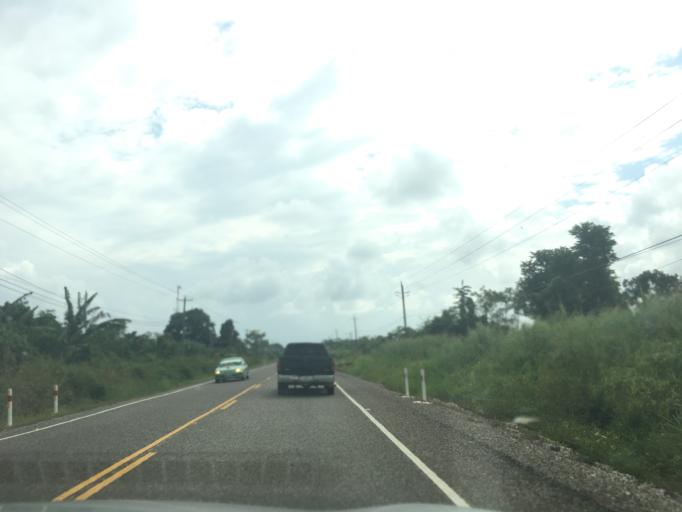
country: BZ
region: Stann Creek
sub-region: Dangriga
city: Dangriga
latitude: 16.9957
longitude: -88.3014
